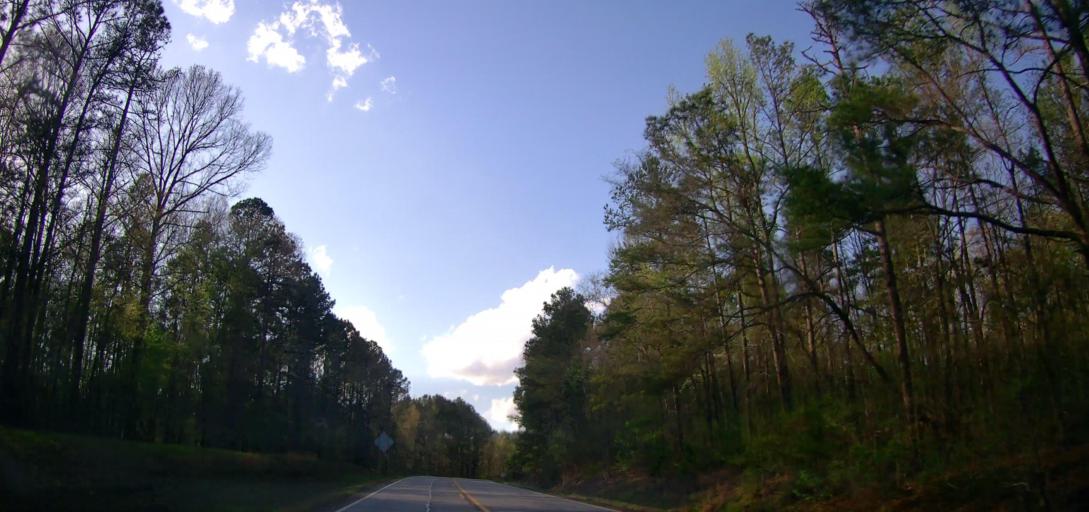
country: US
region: Georgia
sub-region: Putnam County
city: Eatonton
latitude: 33.1832
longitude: -83.4123
